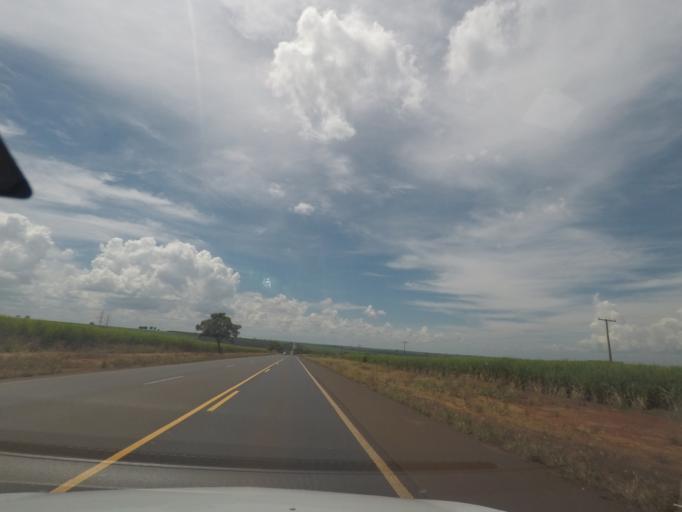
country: BR
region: Sao Paulo
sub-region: Barretos
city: Barretos
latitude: -20.2709
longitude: -48.6730
